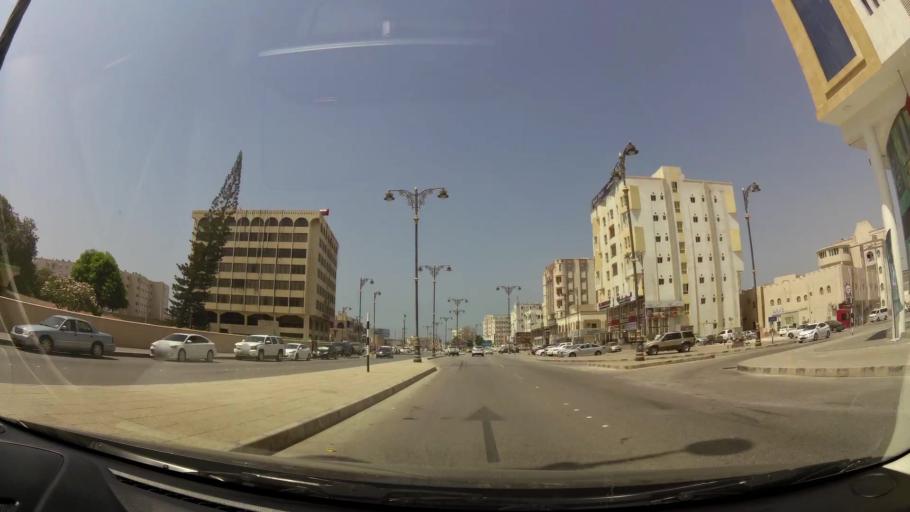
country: OM
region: Zufar
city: Salalah
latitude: 17.0218
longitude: 54.1110
